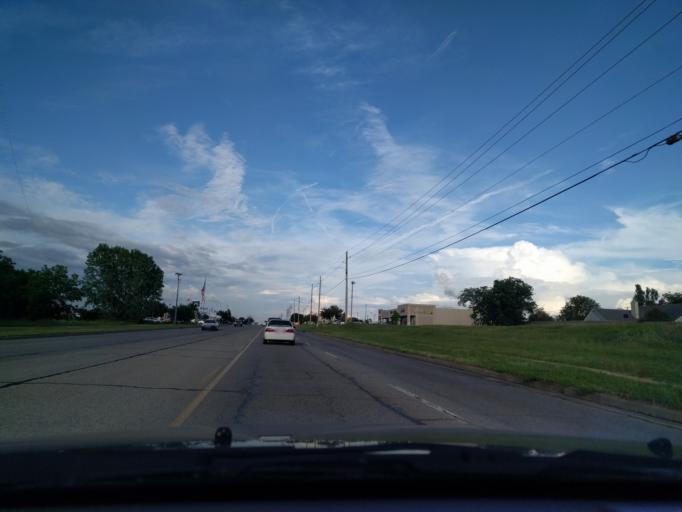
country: US
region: Oklahoma
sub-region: Tulsa County
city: Broken Arrow
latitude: 36.0609
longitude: -95.8225
